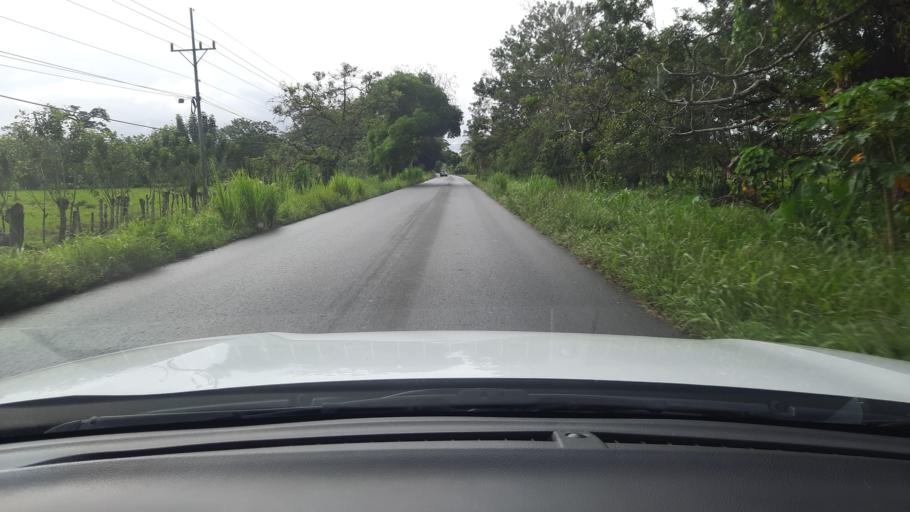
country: CR
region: Alajuela
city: Upala
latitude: 10.9242
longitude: -85.0691
